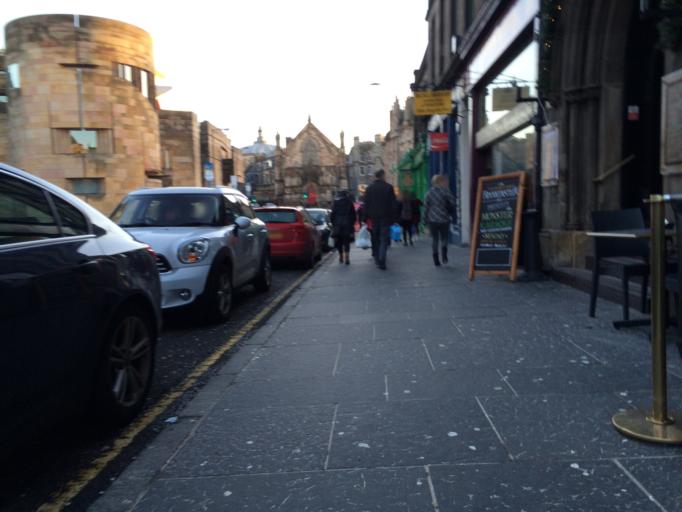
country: GB
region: Scotland
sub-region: Edinburgh
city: Edinburgh
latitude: 55.9474
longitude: -3.1915
